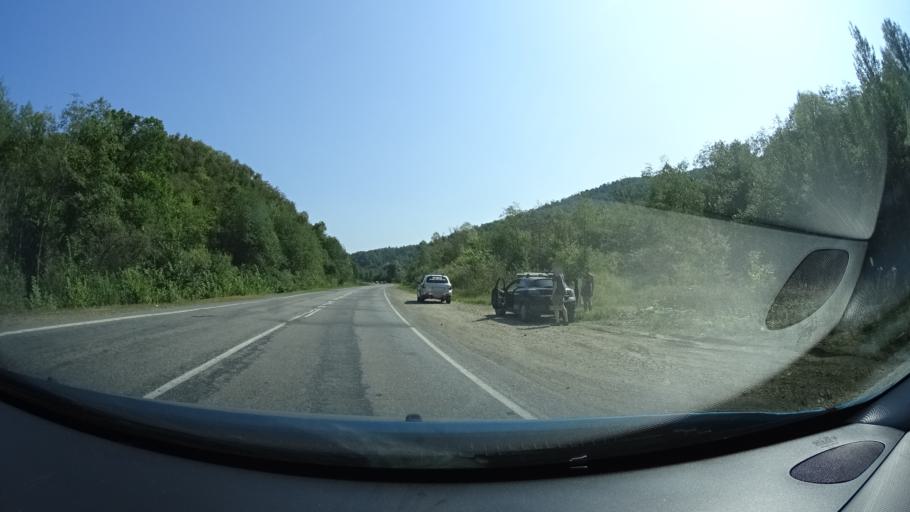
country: RU
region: Bashkortostan
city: Inzer
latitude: 54.3394
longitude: 57.0895
